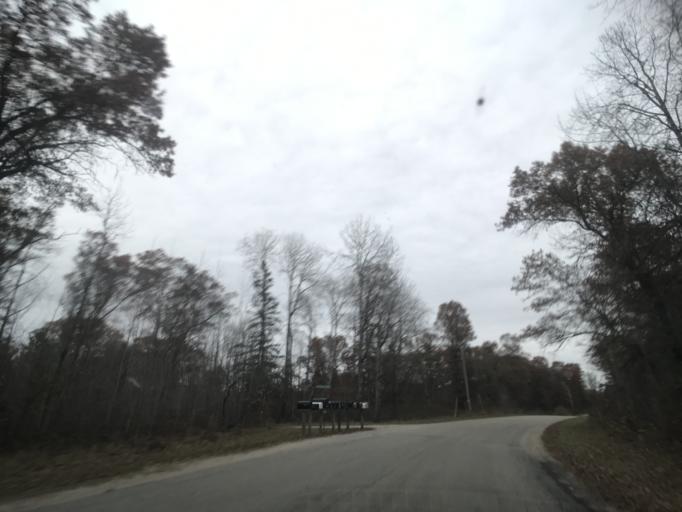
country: US
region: Wisconsin
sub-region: Oconto County
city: Gillett
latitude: 45.3312
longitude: -88.2789
